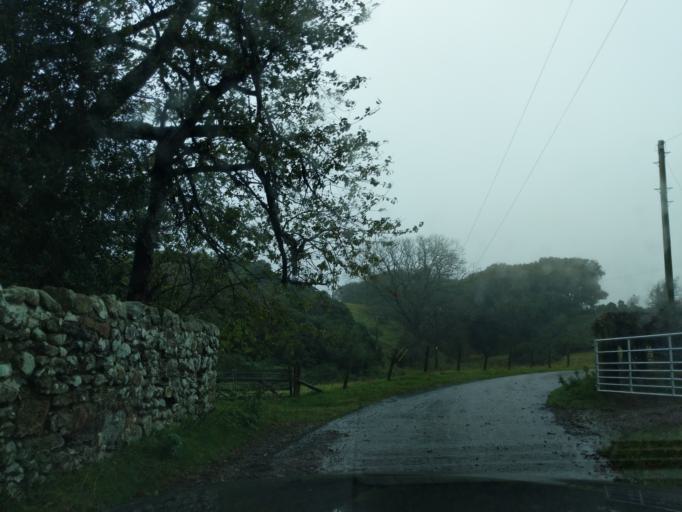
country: GB
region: Scotland
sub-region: East Lothian
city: Dunbar
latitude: 55.9264
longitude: -2.4349
